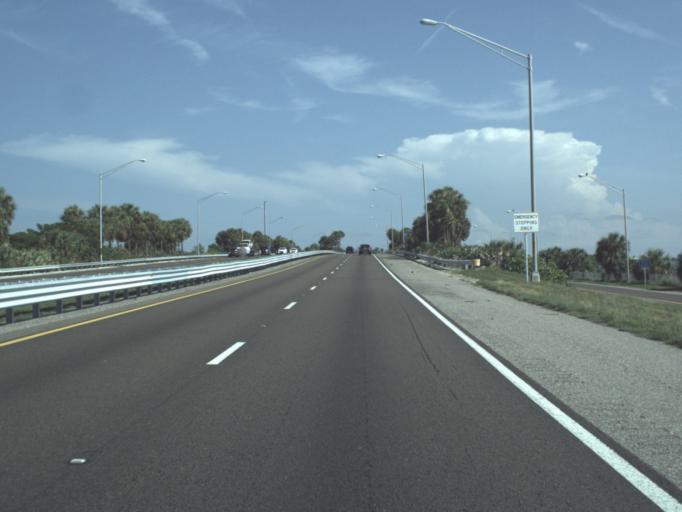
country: US
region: Florida
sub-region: Pinellas County
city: Tierra Verde
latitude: 27.6471
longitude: -82.6738
